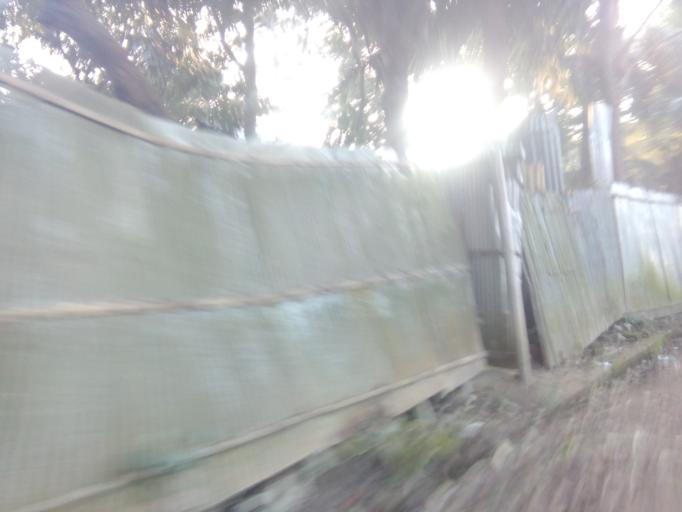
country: BD
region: Chittagong
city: Comilla
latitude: 23.4177
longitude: 91.2127
